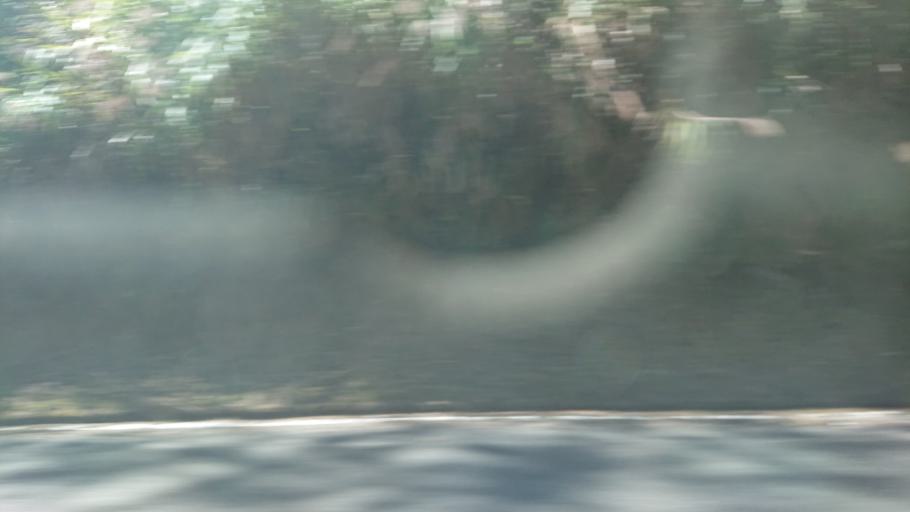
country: TW
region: Taiwan
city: Lugu
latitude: 23.4830
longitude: 120.8549
